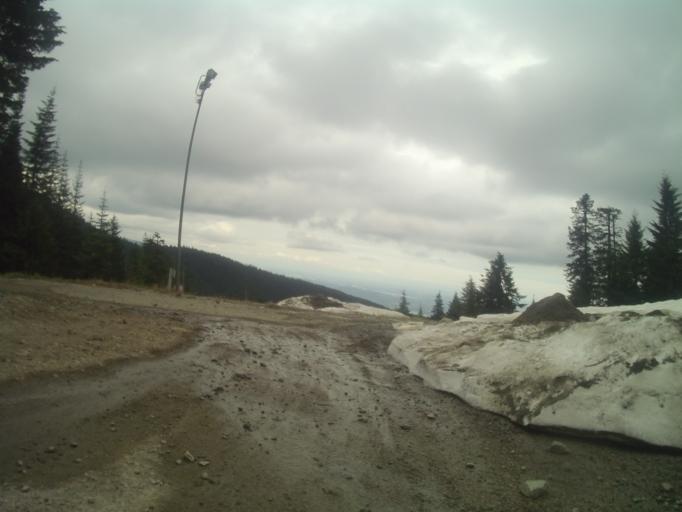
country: CA
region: British Columbia
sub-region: Fraser Valley Regional District
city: North Vancouver
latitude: 49.3793
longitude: -123.0757
